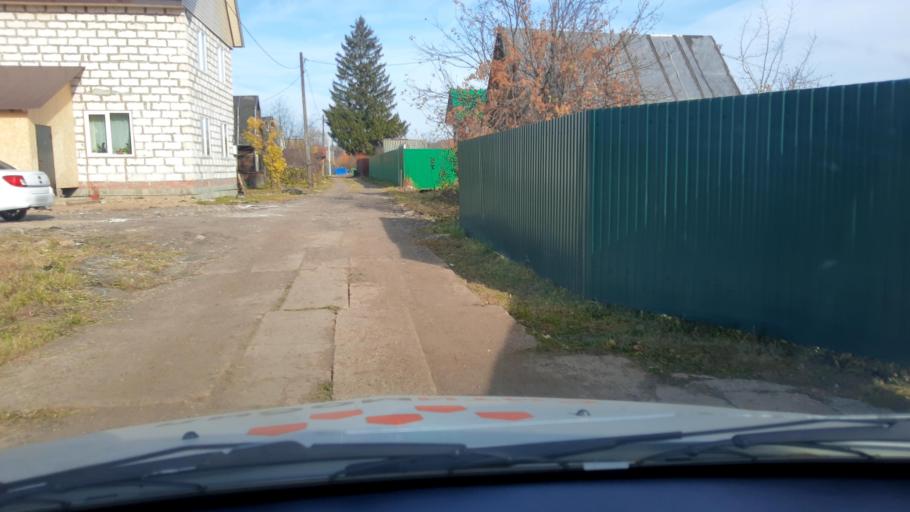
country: RU
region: Bashkortostan
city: Ufa
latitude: 54.8108
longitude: 56.1506
